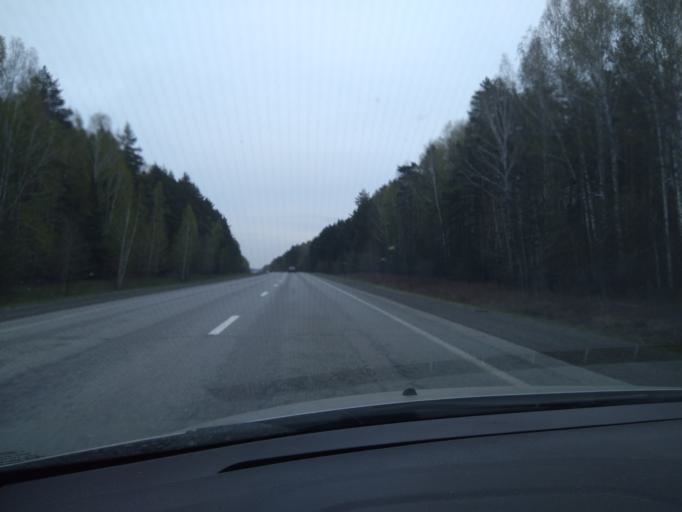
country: RU
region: Sverdlovsk
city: Baraba
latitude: 56.7812
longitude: 61.7818
